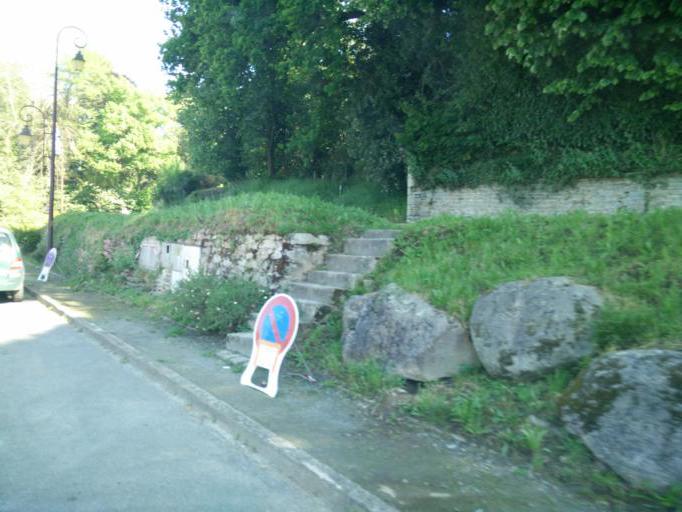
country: FR
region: Brittany
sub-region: Departement du Morbihan
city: Josselin
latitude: 47.9507
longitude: -2.5452
